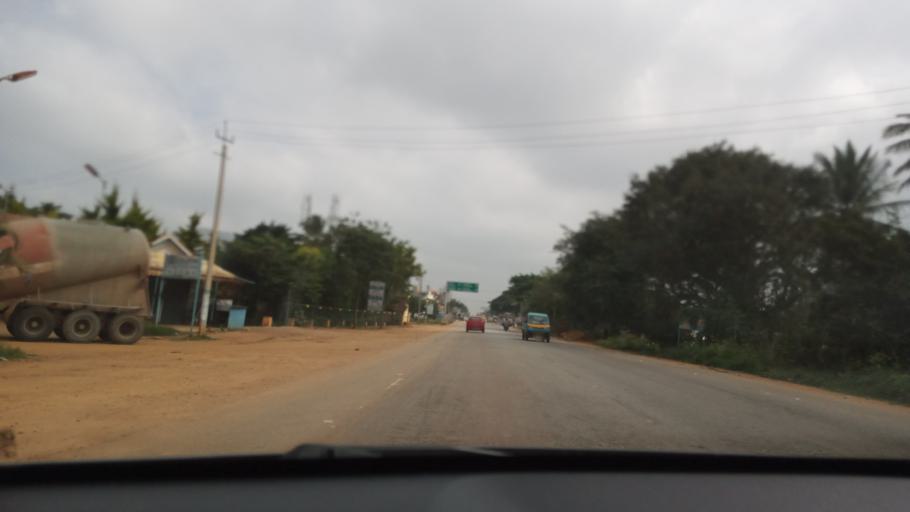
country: IN
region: Karnataka
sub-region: Chikkaballapur
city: Chintamani
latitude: 13.3253
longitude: 77.9903
